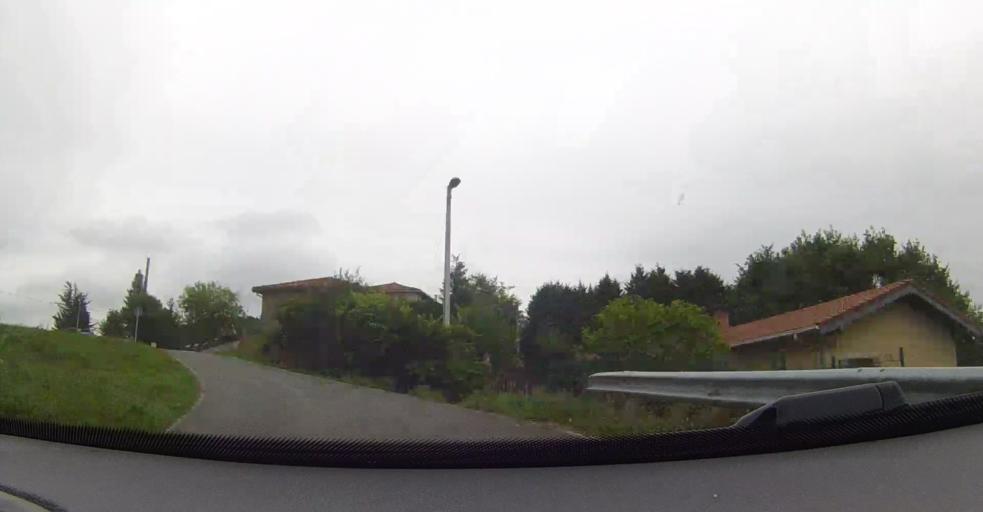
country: ES
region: Basque Country
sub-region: Bizkaia
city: Urrestieta
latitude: 43.2342
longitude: -3.1870
